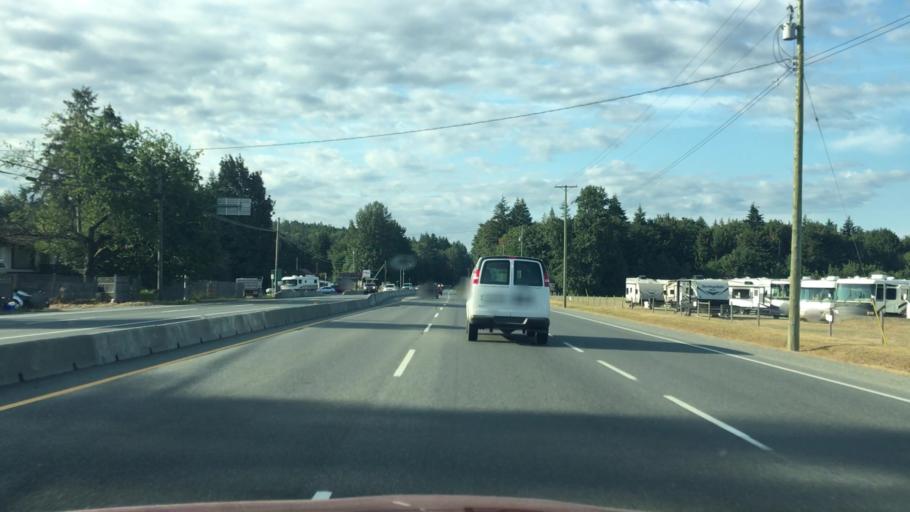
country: CA
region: British Columbia
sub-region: Cowichan Valley Regional District
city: Ladysmith
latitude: 49.0545
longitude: -123.8774
